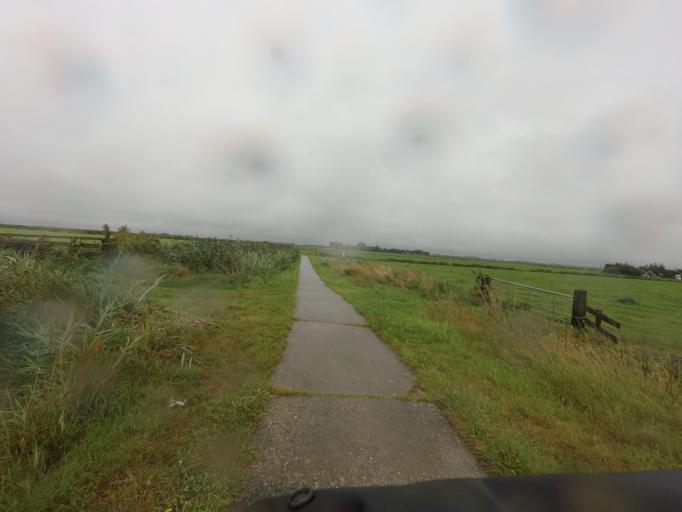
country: NL
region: Friesland
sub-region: Sudwest Fryslan
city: Workum
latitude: 52.9923
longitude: 5.4986
